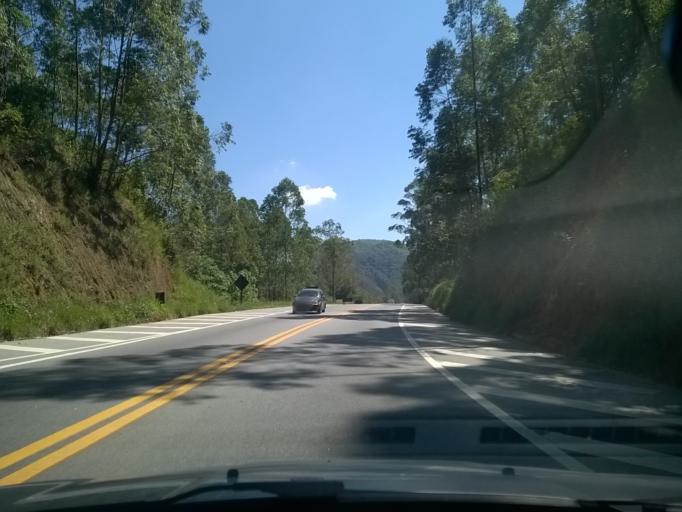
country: BR
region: Sao Paulo
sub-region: Varzea Paulista
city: Varzea Paulista
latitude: -23.2743
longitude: -46.8114
